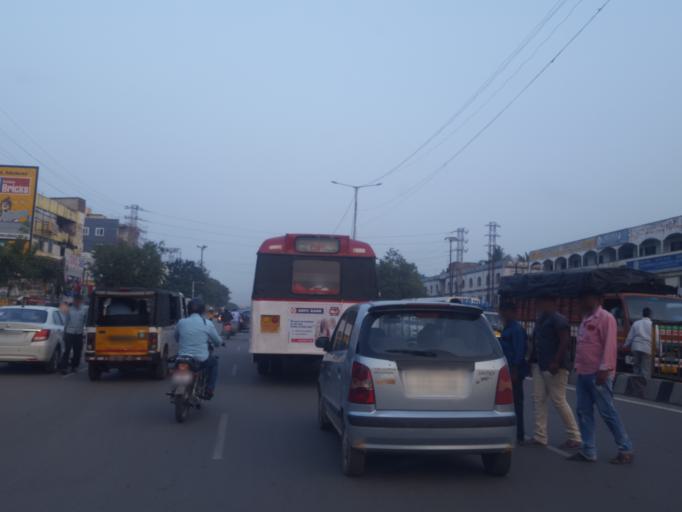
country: IN
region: Telangana
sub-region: Medak
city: Serilingampalle
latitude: 17.4952
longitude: 78.3181
